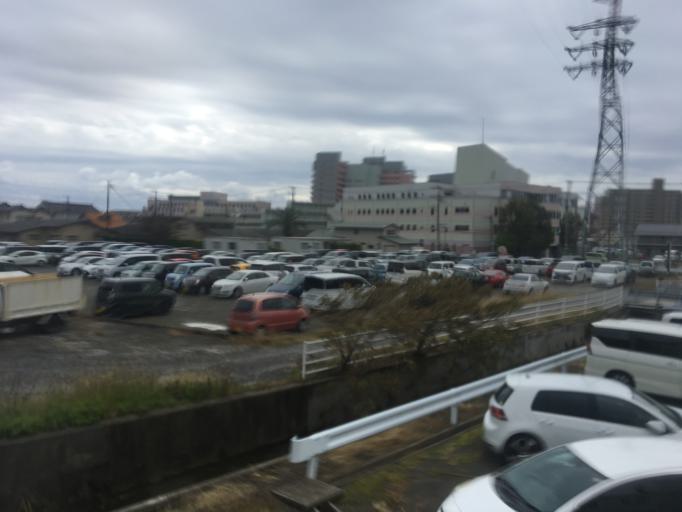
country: JP
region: Chiba
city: Kawaguchi
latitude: 35.1239
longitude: 140.1244
